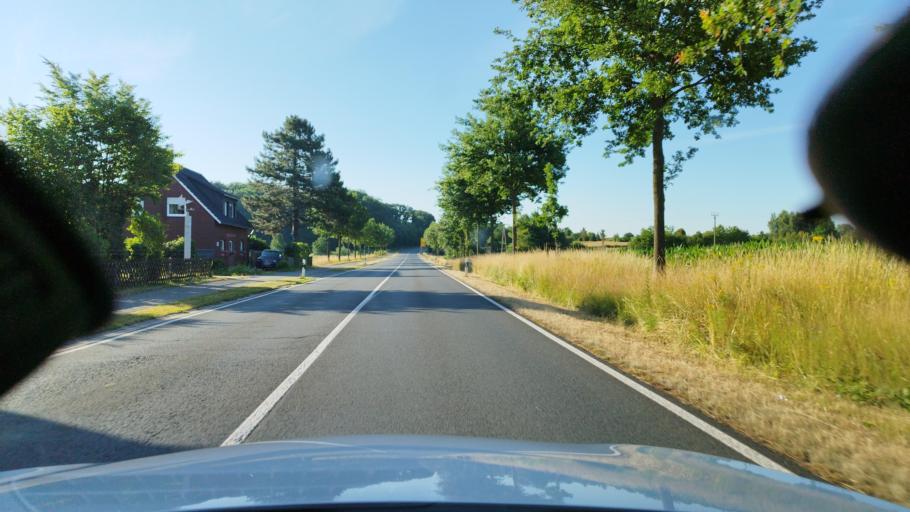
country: DE
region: North Rhine-Westphalia
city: Selm
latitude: 51.6591
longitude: 7.4974
